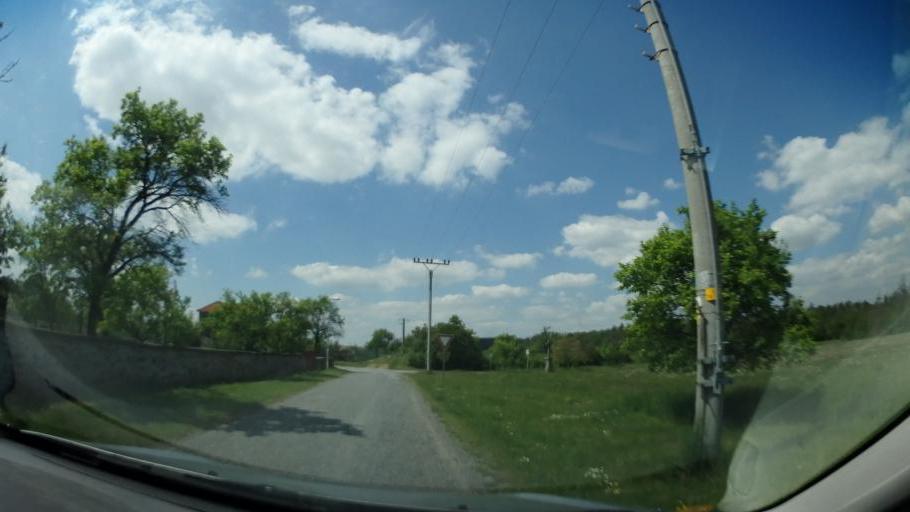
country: CZ
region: Vysocina
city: Hrotovice
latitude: 49.1554
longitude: 16.0776
